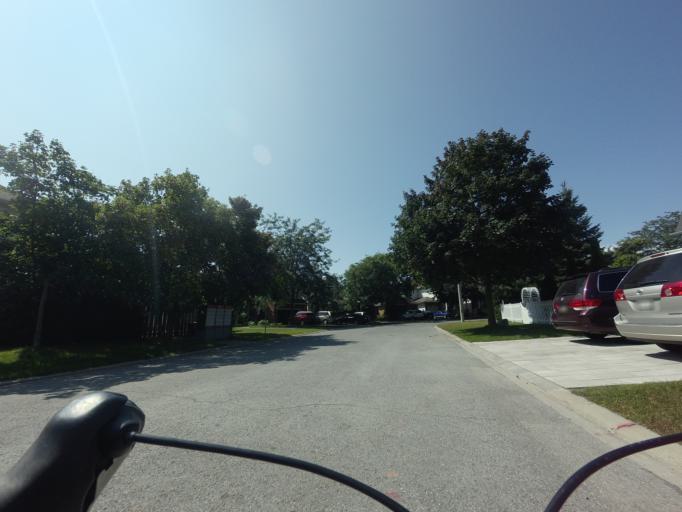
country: CA
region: Ontario
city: Bells Corners
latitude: 45.2843
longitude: -75.8514
